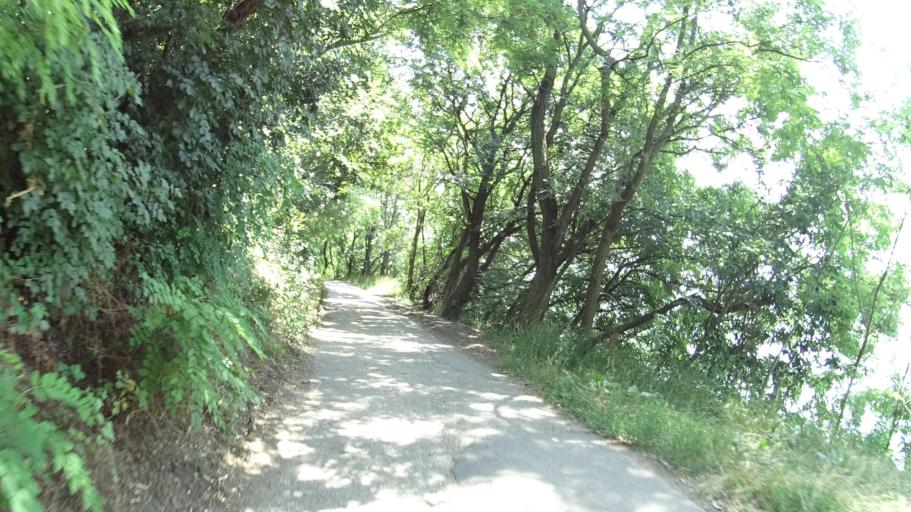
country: HU
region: Veszprem
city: Tihany
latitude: 46.9024
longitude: 17.8529
